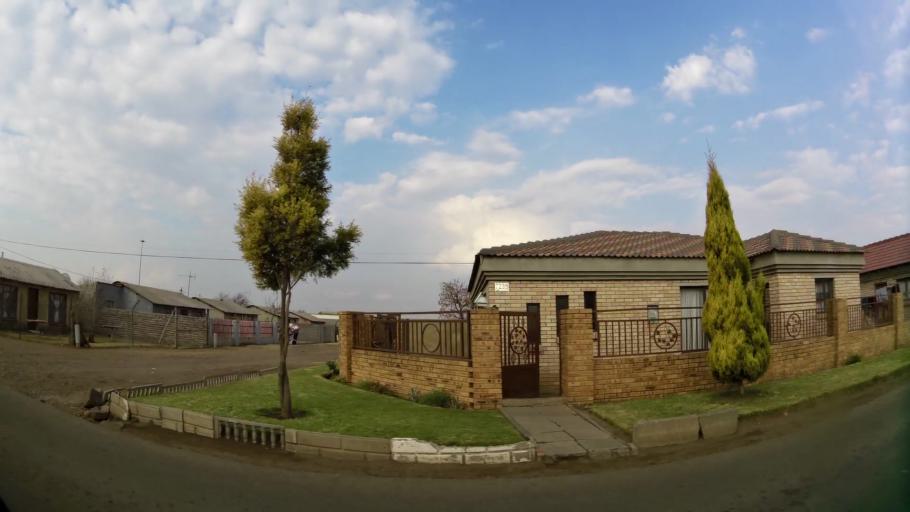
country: ZA
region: Gauteng
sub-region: Sedibeng District Municipality
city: Vanderbijlpark
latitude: -26.6903
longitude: 27.8799
